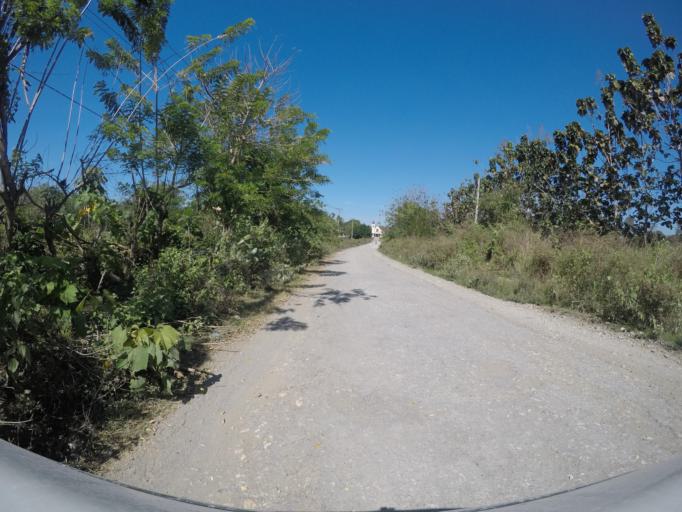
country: TL
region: Viqueque
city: Viqueque
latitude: -8.9743
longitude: 126.0526
